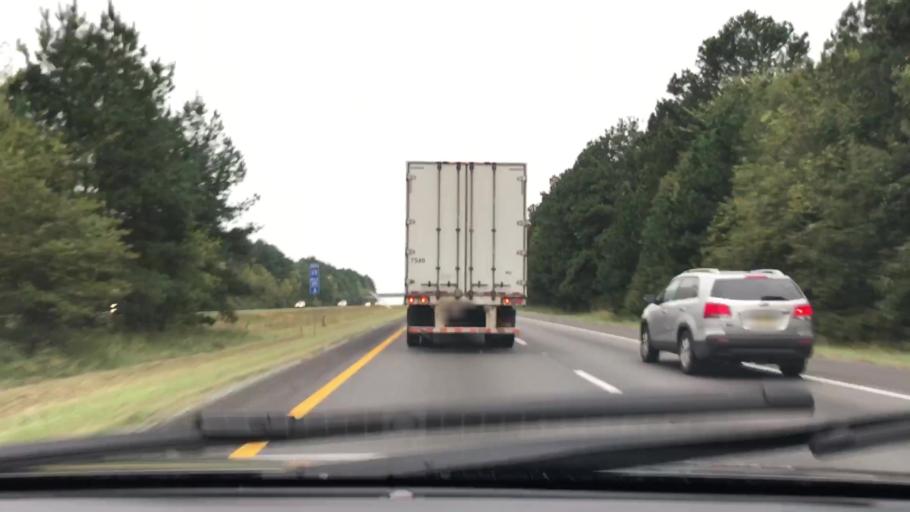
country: US
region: Tennessee
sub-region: Sumner County
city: White House
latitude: 36.4399
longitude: -86.7041
